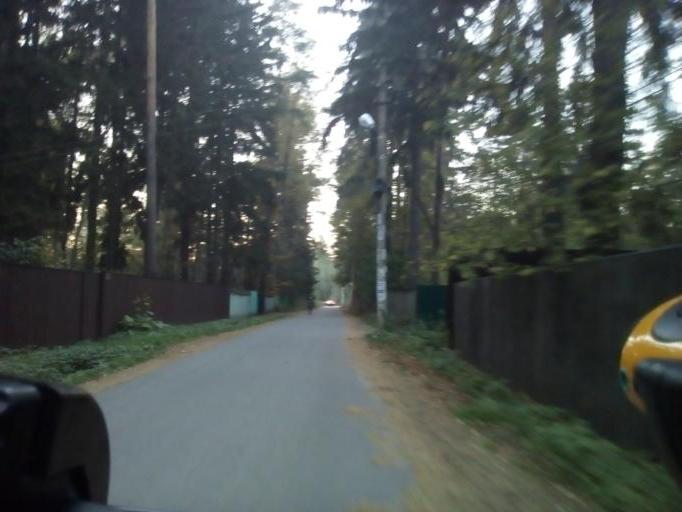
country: RU
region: Moskovskaya
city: Kratovo
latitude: 55.5927
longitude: 38.2004
